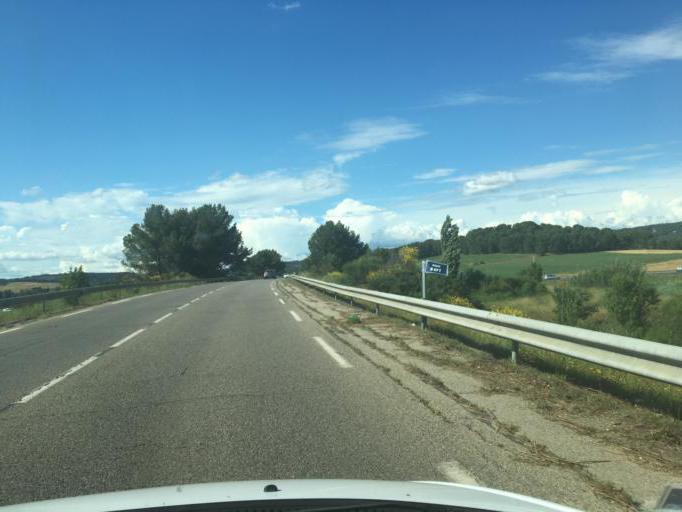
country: FR
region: Provence-Alpes-Cote d'Azur
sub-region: Departement des Bouches-du-Rhone
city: Eguilles
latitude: 43.5357
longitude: 5.3485
